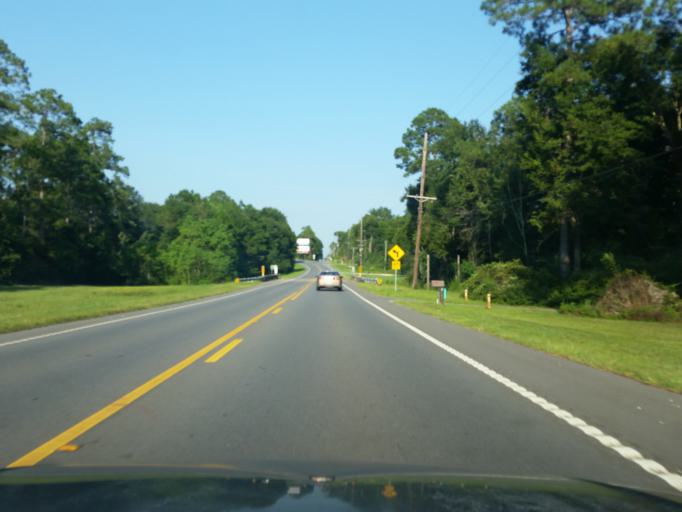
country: US
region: Alabama
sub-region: Baldwin County
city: Elberta
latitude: 30.4069
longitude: -87.6259
